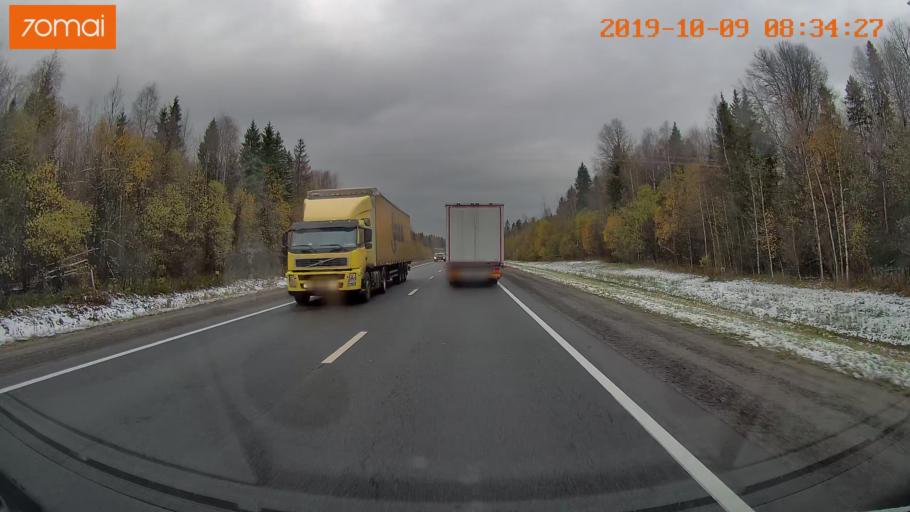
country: RU
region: Vologda
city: Gryazovets
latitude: 58.8969
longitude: 40.1856
